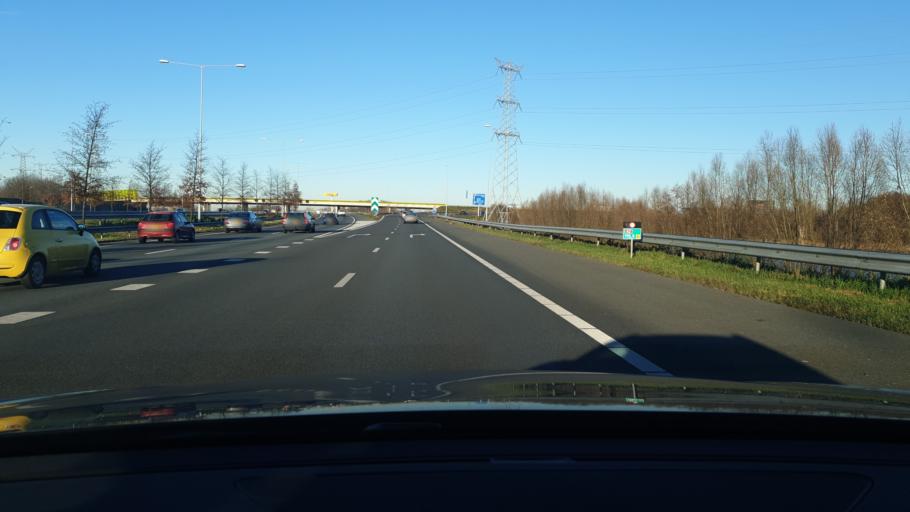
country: NL
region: North Brabant
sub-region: Gemeente 's-Hertogenbosch
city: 's-Hertogenbosch
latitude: 51.6951
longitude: 5.3520
